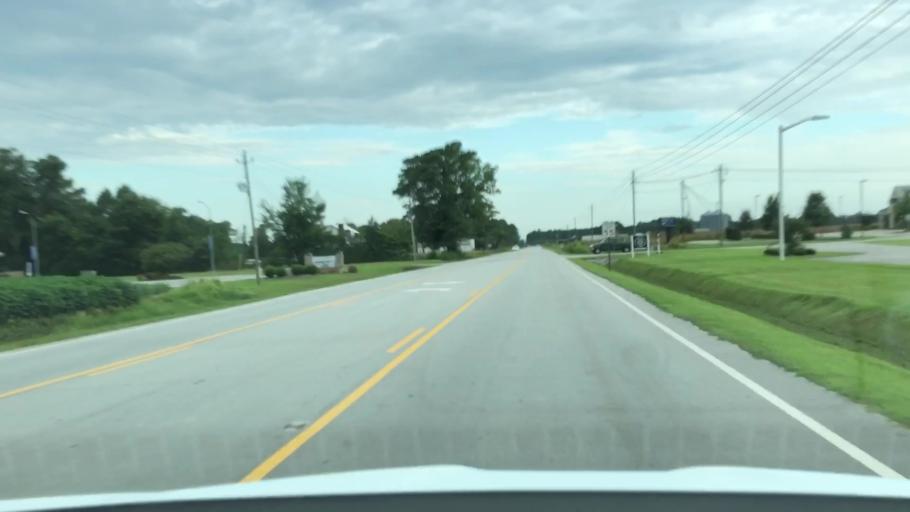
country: US
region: North Carolina
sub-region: Jones County
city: Trenton
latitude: 35.0678
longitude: -77.3660
